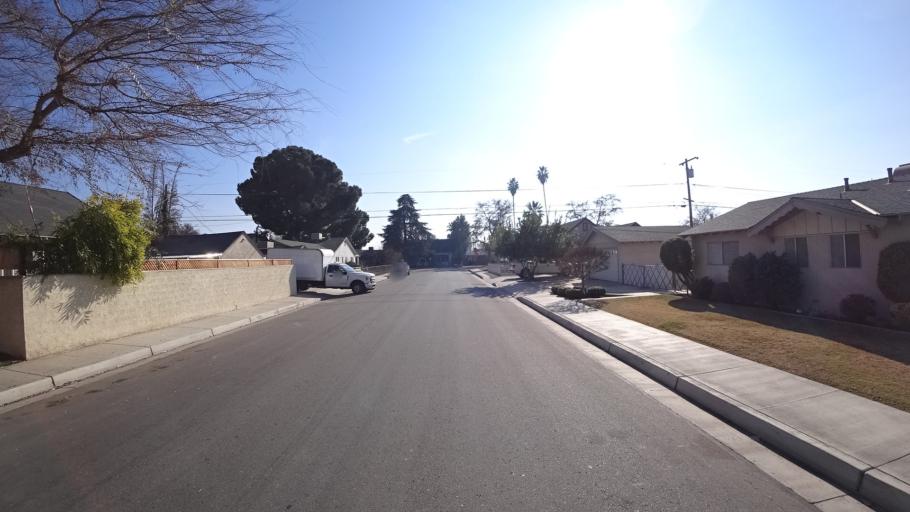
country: US
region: California
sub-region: Kern County
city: Bakersfield
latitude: 35.3656
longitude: -119.0365
